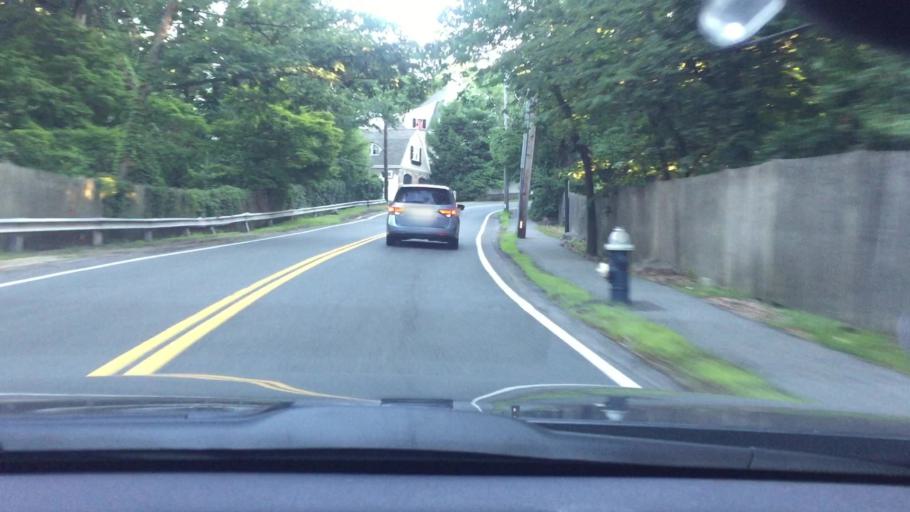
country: US
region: Massachusetts
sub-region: Suffolk County
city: Jamaica Plain
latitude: 42.3164
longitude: -71.1306
